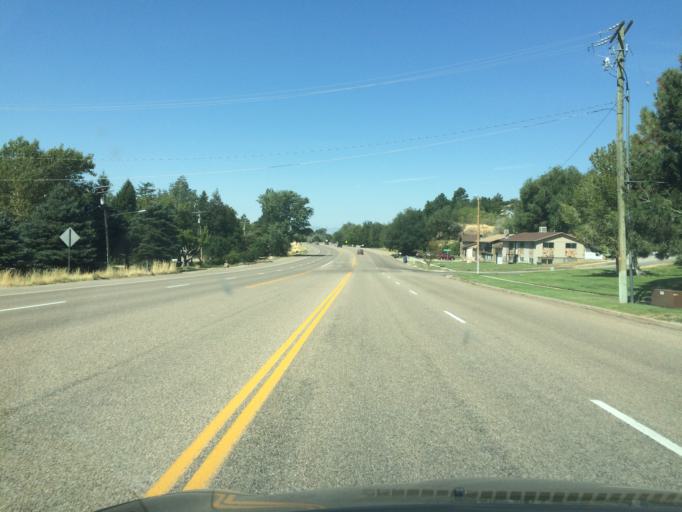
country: US
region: Utah
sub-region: Weber County
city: Ogden
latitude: 41.2397
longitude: -111.9356
